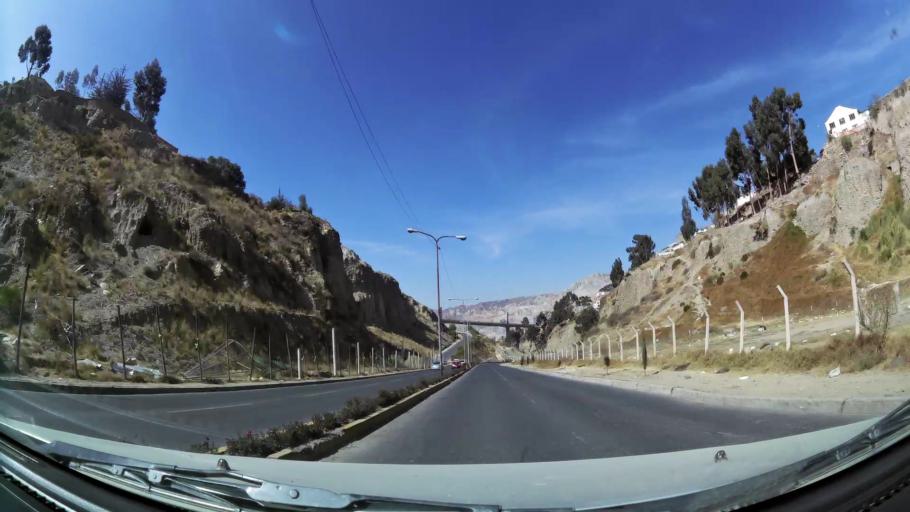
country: BO
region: La Paz
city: La Paz
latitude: -16.5101
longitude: -68.1159
